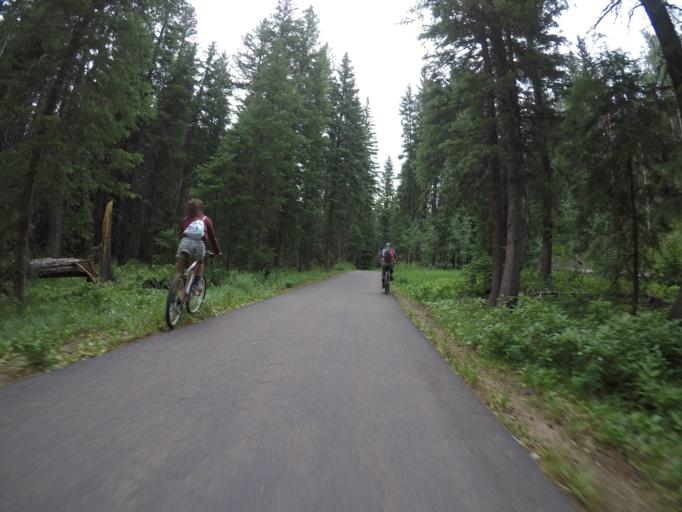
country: US
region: Colorado
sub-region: Grand County
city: Fraser
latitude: 39.8999
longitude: -105.7756
